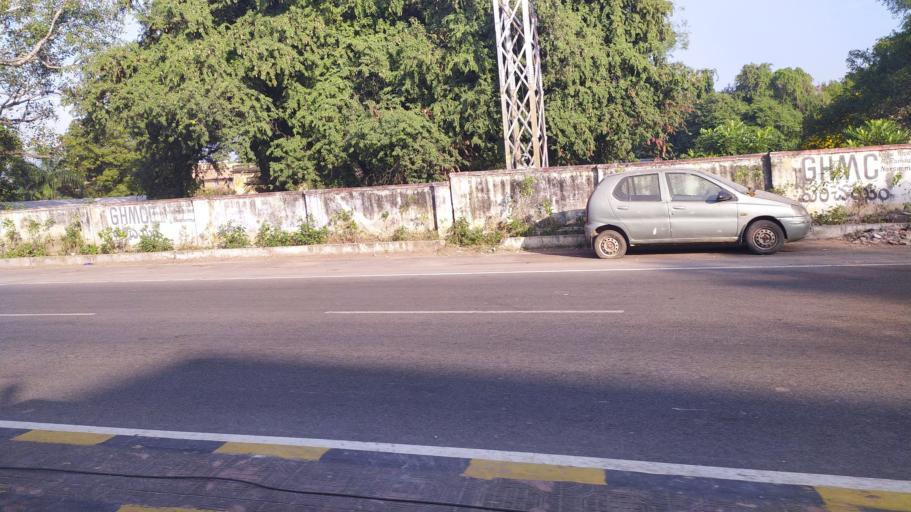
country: IN
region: Telangana
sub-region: Hyderabad
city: Hyderabad
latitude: 17.3215
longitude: 78.4004
